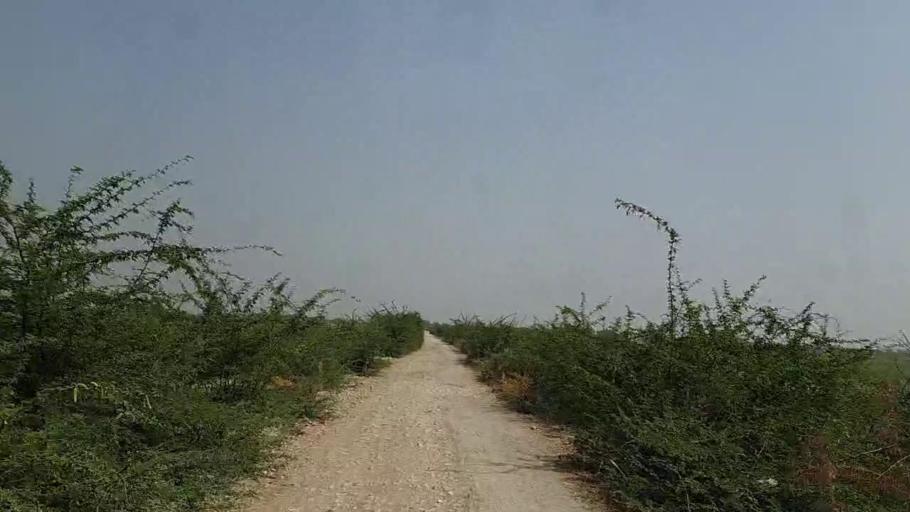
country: PK
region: Sindh
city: Naukot
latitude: 24.8097
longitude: 69.3726
